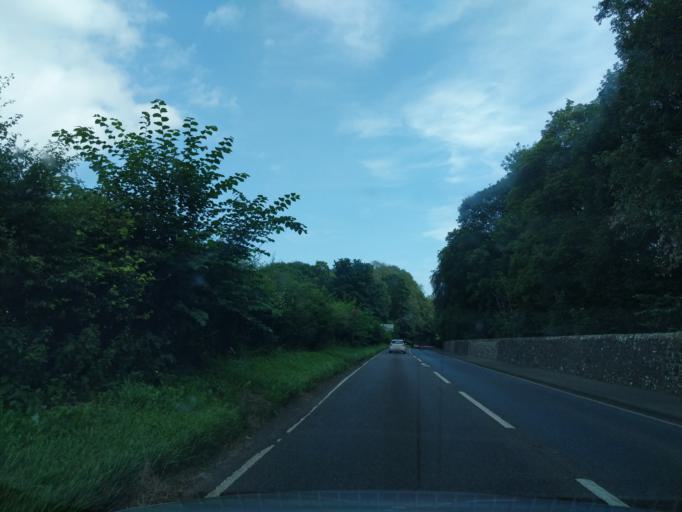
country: GB
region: Scotland
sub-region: Angus
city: Muirhead
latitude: 56.4845
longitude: -3.0280
